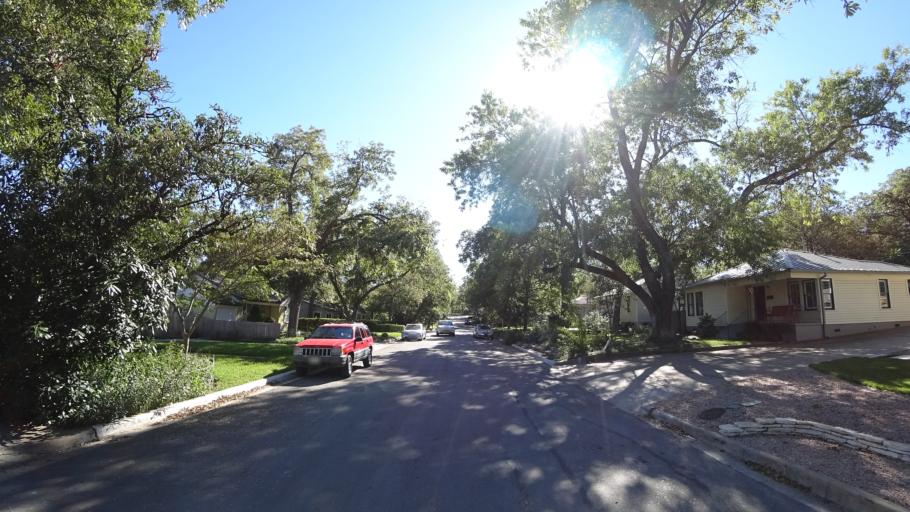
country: US
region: Texas
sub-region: Travis County
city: Austin
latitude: 30.3130
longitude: -97.7503
